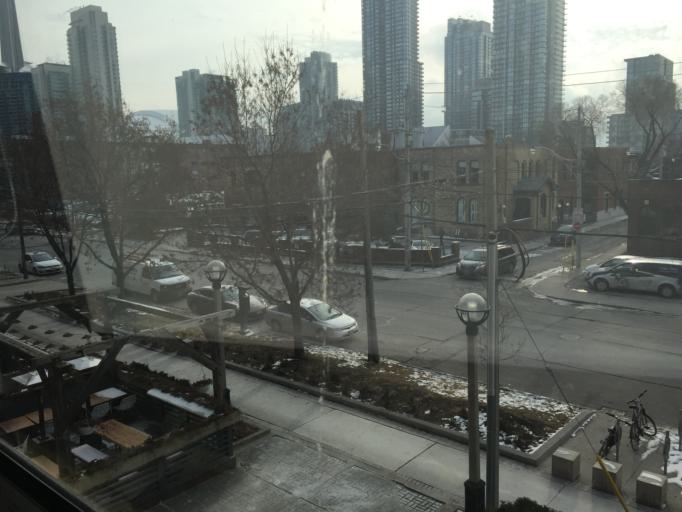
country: CA
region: Ontario
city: Toronto
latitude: 43.6433
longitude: -79.3982
